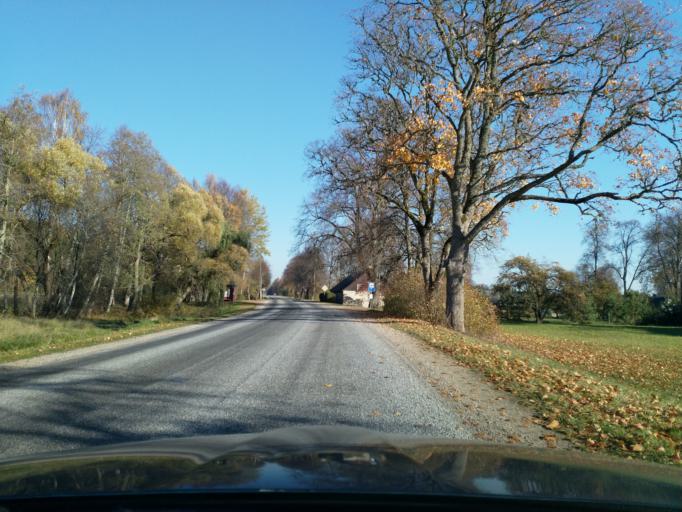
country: LV
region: Skrunda
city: Skrunda
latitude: 56.7763
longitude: 21.9900
